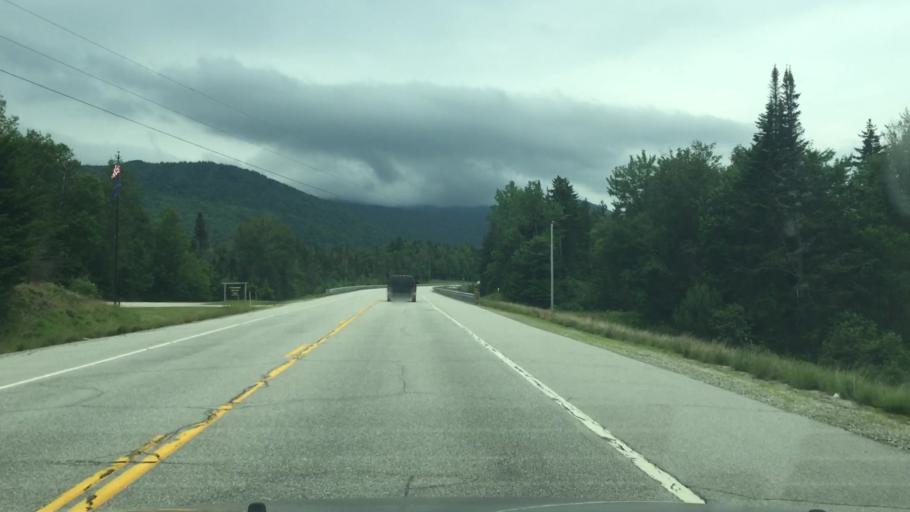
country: US
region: New Hampshire
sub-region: Coos County
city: Jefferson
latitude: 44.2396
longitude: -71.4261
